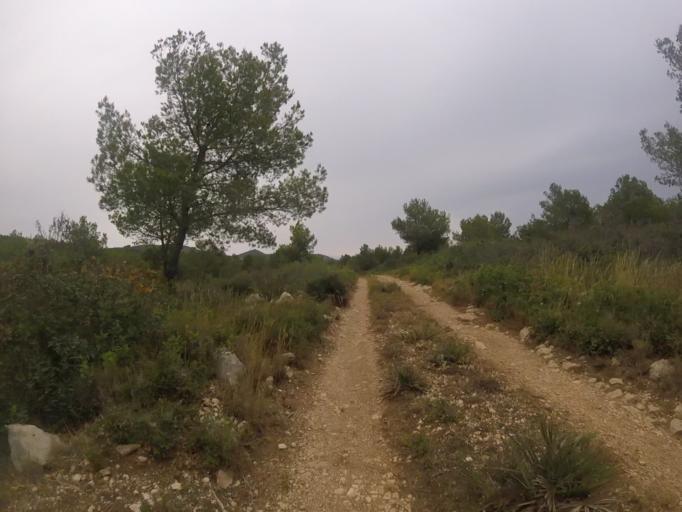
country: ES
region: Valencia
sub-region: Provincia de Castello
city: Alcoceber
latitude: 40.2848
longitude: 0.2847
